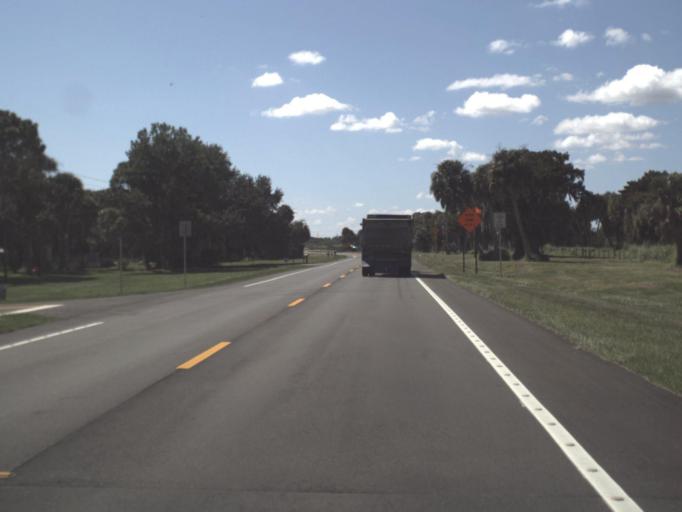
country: US
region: Florida
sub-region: Glades County
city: Moore Haven
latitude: 27.0029
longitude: -81.0614
